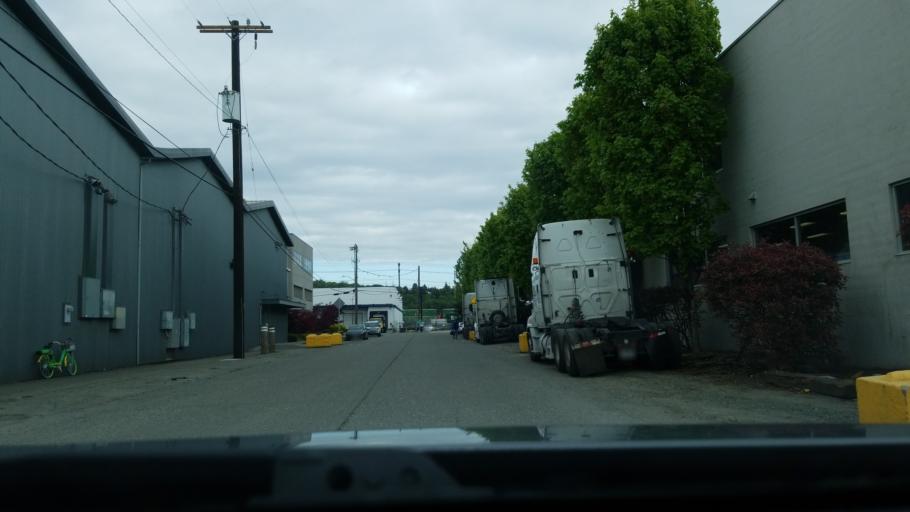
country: US
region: Washington
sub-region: King County
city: White Center
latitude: 47.5574
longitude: -122.3324
